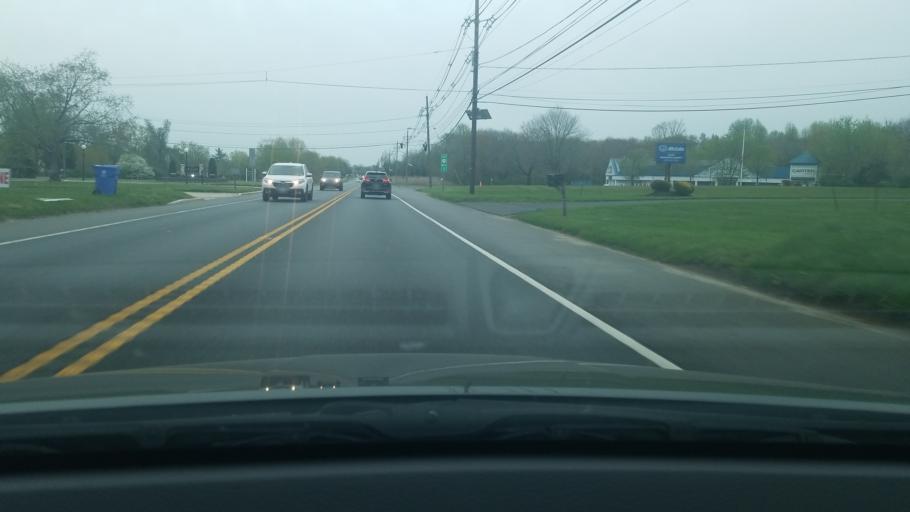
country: US
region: New Jersey
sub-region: Burlington County
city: Medford Lakes
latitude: 39.9005
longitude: -74.8414
